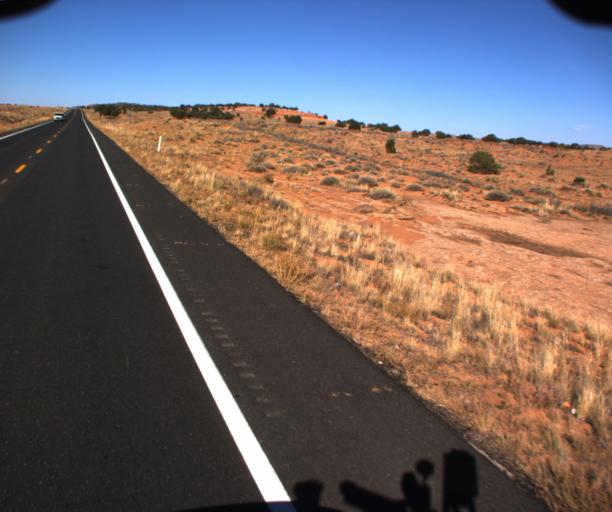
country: US
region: Arizona
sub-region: Coconino County
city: Kaibito
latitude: 36.5119
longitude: -110.7045
